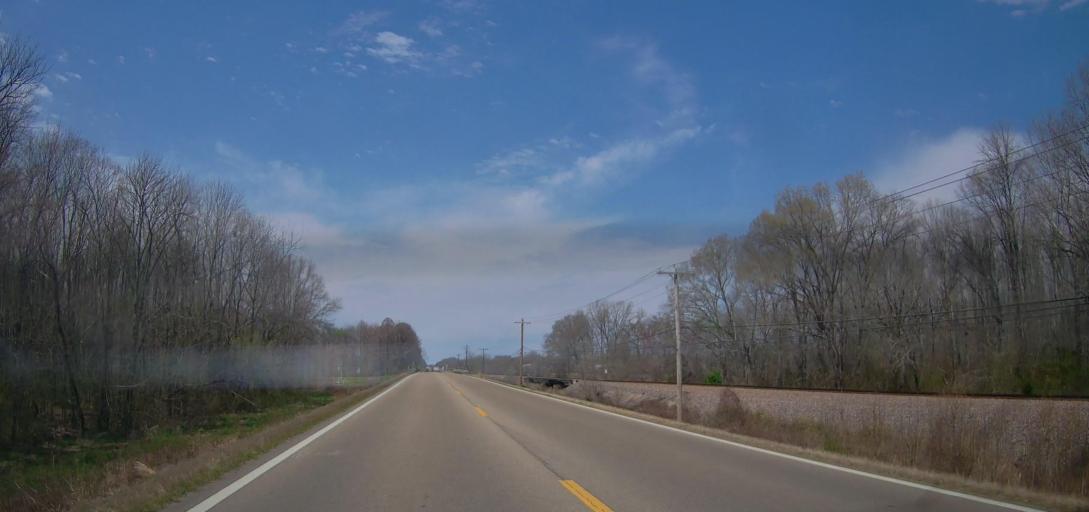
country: US
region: Mississippi
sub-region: Union County
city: New Albany
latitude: 34.5175
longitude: -89.0491
